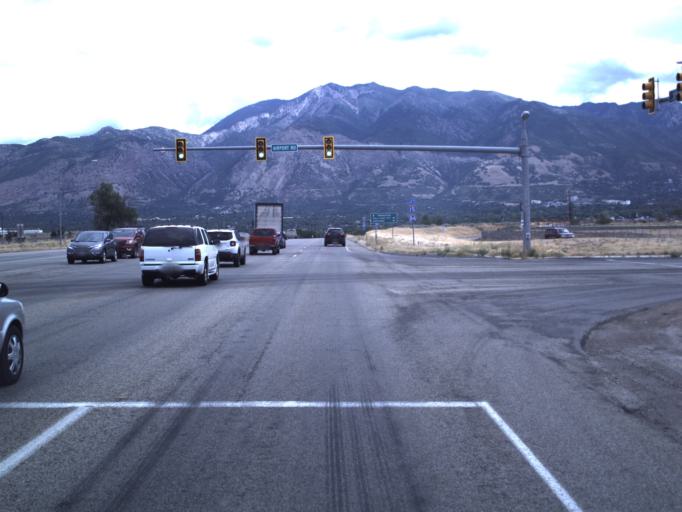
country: US
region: Utah
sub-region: Weber County
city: Riverdale
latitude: 41.2050
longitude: -112.0023
